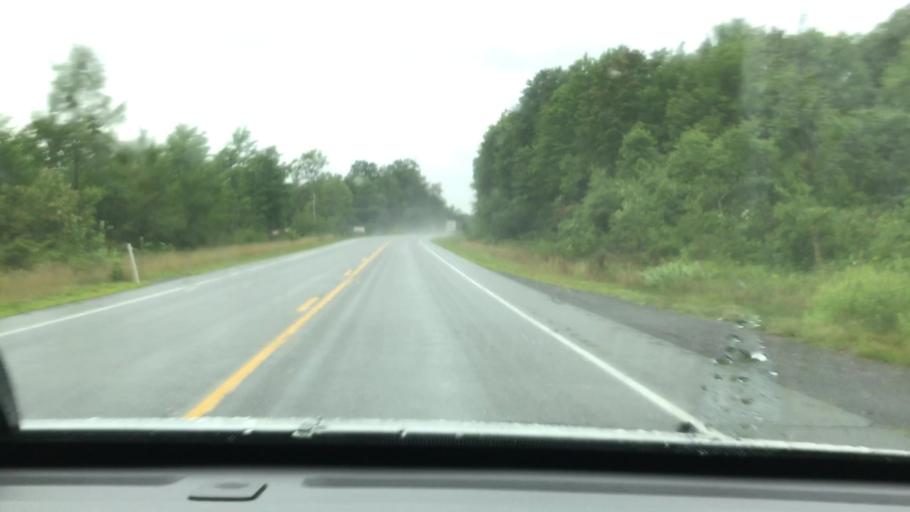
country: US
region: Pennsylvania
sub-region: Clearfield County
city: Osceola Mills
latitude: 40.8295
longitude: -78.2249
